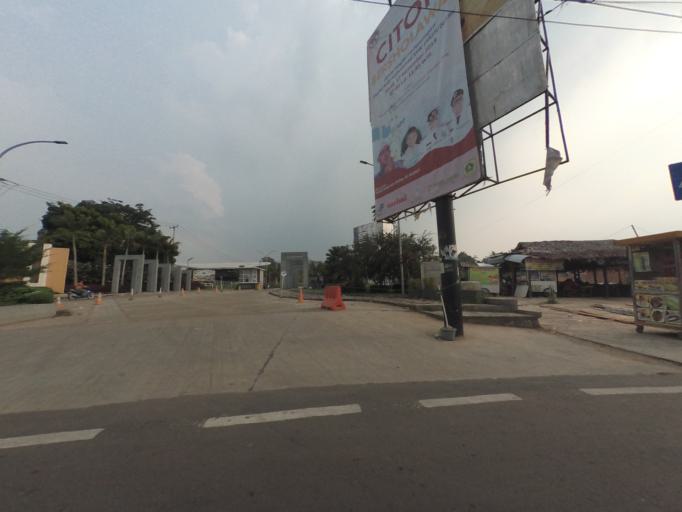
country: ID
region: West Java
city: Ciampea
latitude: -6.5744
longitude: 106.6657
